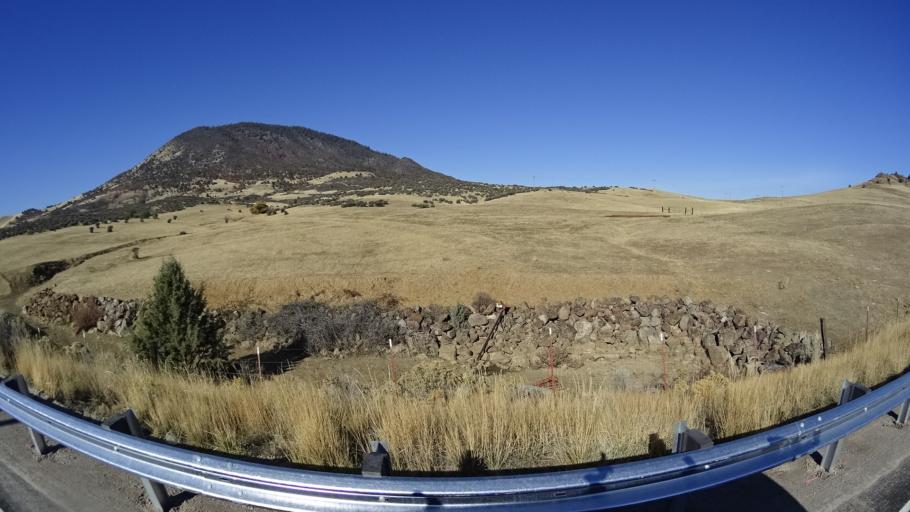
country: US
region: California
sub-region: Siskiyou County
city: Montague
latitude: 41.8471
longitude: -122.4705
